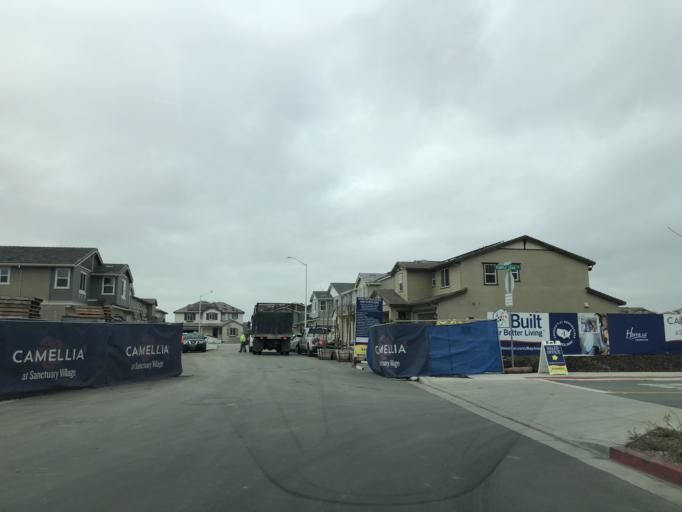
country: US
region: California
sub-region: Alameda County
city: Fremont
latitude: 37.5157
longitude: -122.0008
